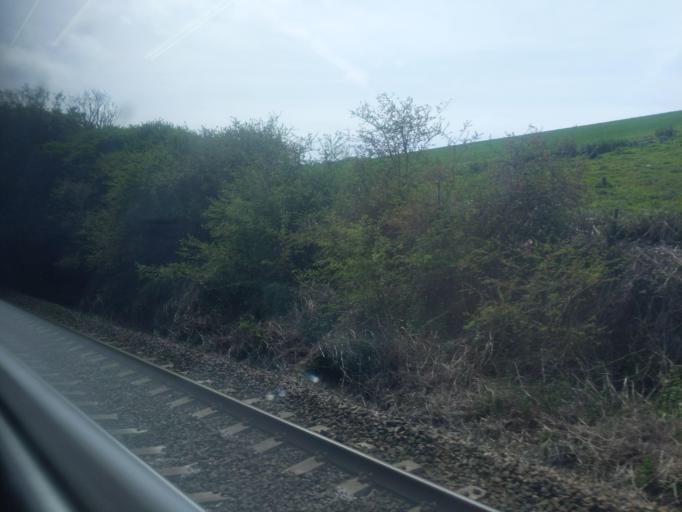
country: GB
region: England
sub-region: Cornwall
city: Marazion
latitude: 50.1414
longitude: -5.4674
